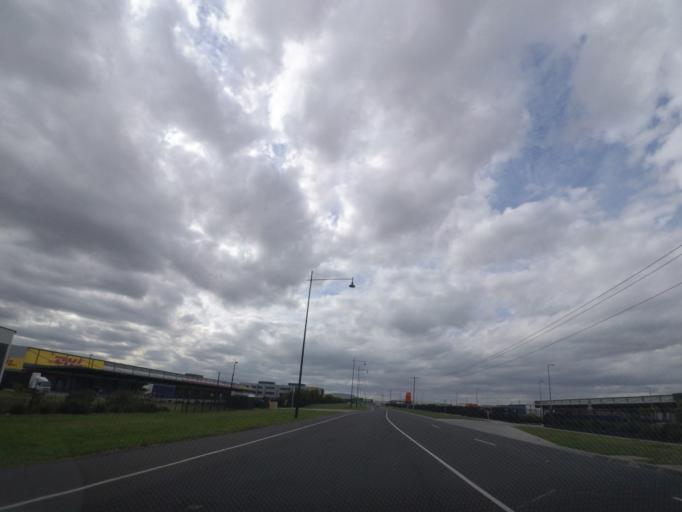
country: AU
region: Victoria
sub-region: Brimbank
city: Keilor Park
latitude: -37.6964
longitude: 144.8566
